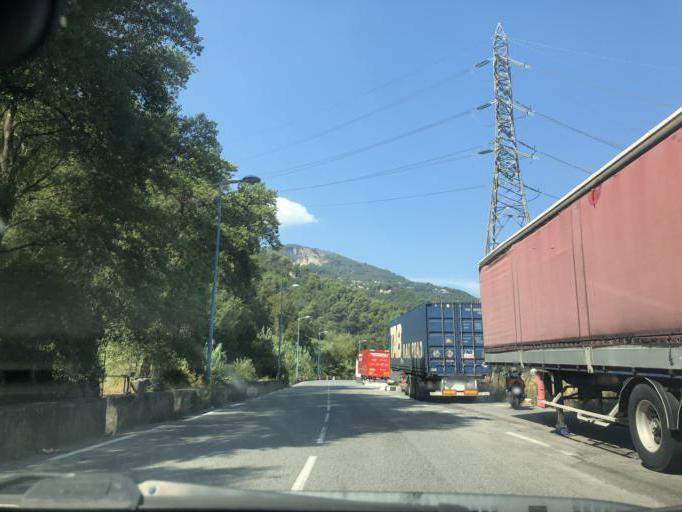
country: FR
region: Provence-Alpes-Cote d'Azur
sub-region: Departement des Alpes-Maritimes
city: Carros
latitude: 43.8020
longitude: 7.1913
